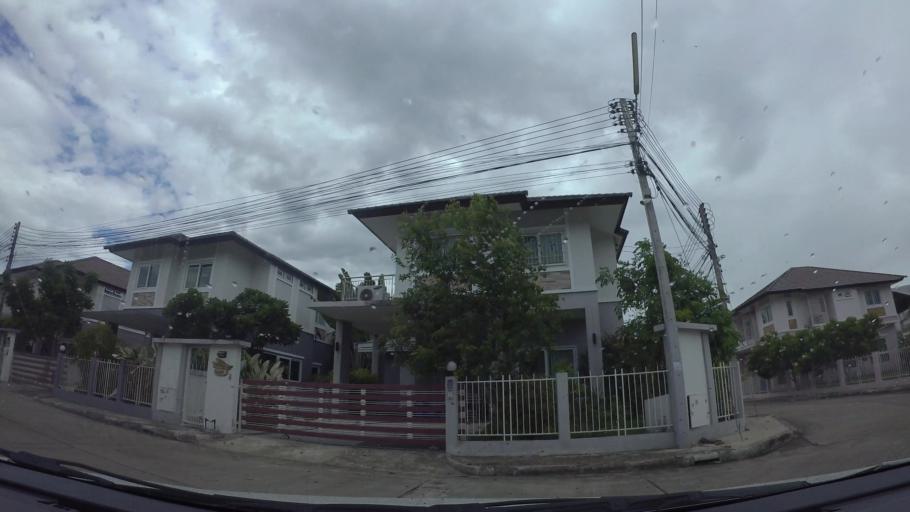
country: TH
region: Chiang Mai
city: Saraphi
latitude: 18.7492
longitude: 99.0491
